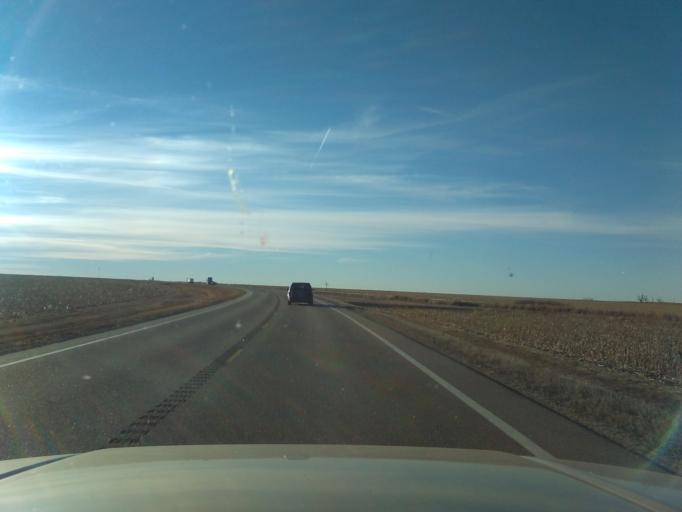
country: US
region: Kansas
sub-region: Thomas County
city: Colby
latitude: 39.4648
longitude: -100.7618
